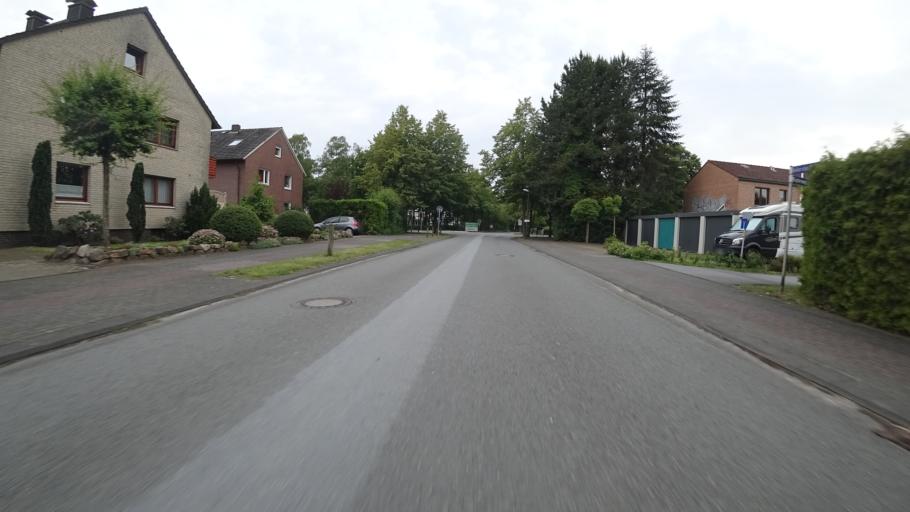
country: DE
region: North Rhine-Westphalia
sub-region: Regierungsbezirk Detmold
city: Guetersloh
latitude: 51.9498
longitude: 8.4046
